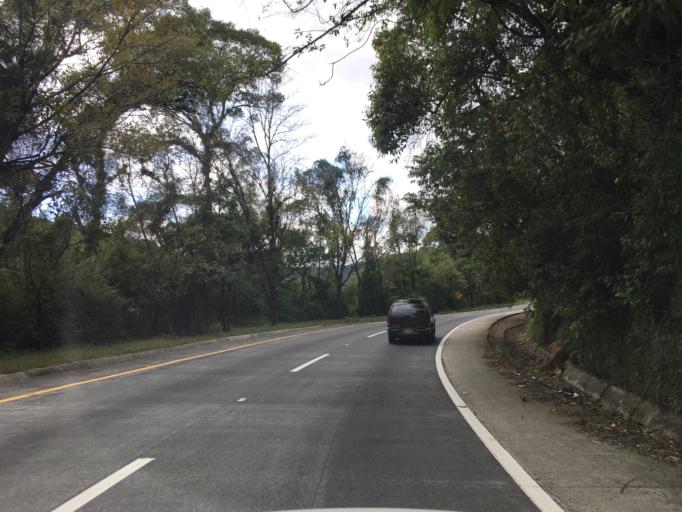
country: GT
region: Sacatepequez
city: Santa Lucia Milpas Altas
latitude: 14.5608
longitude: -90.6916
